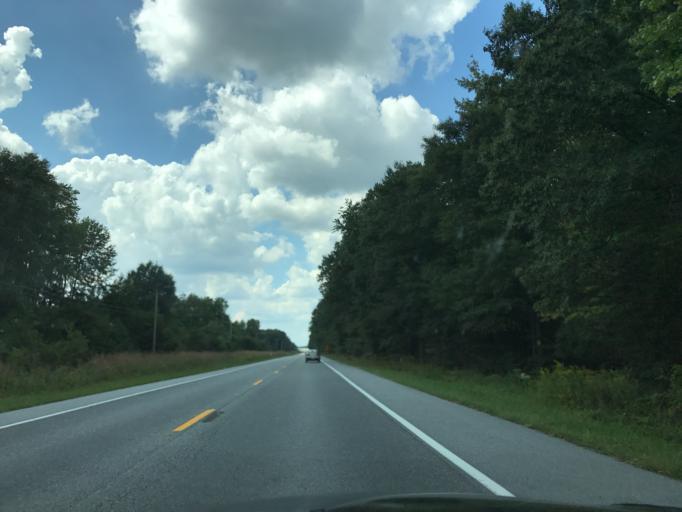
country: US
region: Maryland
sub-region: Caroline County
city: Greensboro
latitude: 39.1448
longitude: -75.8366
